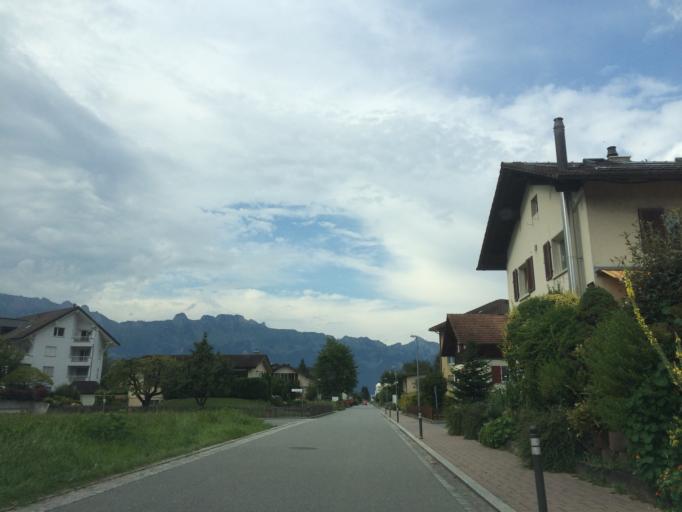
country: LI
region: Schaan
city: Schaan
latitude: 47.1699
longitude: 9.5075
